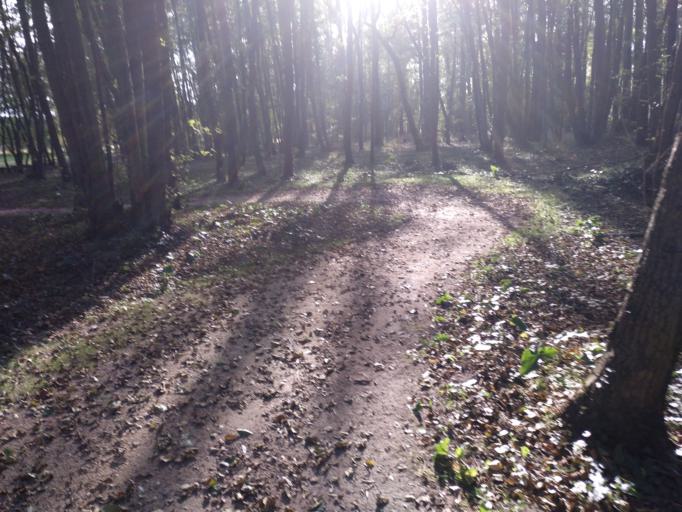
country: FR
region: Rhone-Alpes
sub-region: Departement du Rhone
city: Chaponnay
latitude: 45.6375
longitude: 4.9341
